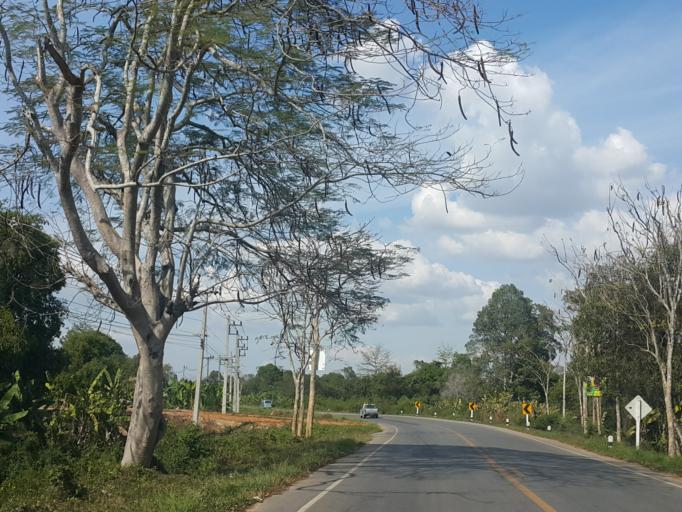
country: TH
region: Sukhothai
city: Sawankhalok
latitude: 17.2467
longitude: 99.8472
